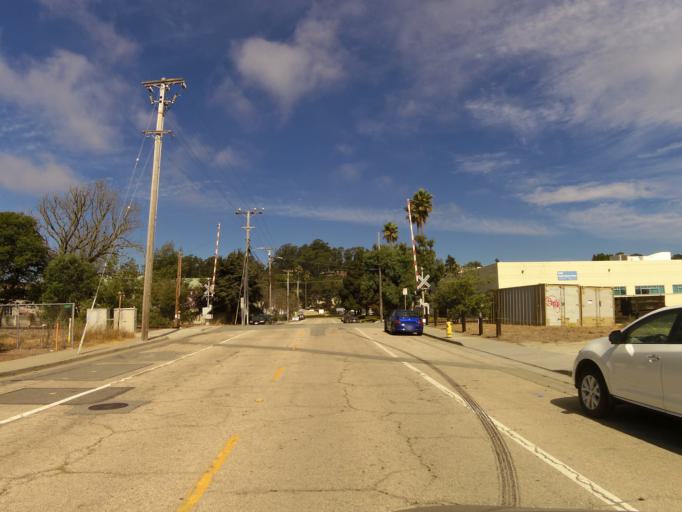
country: US
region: California
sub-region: Santa Cruz County
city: Santa Cruz
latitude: 36.9581
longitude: -122.0574
